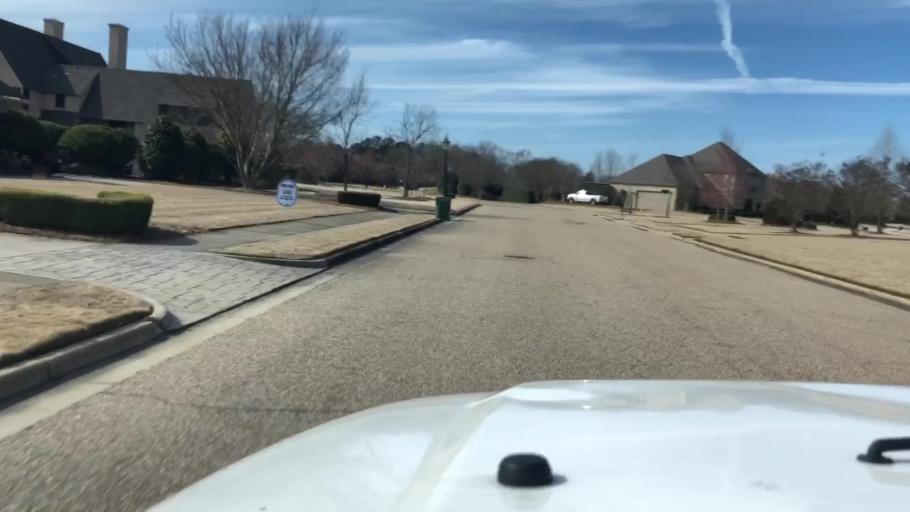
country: US
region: Alabama
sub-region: Montgomery County
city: Pike Road
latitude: 32.3535
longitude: -86.1566
